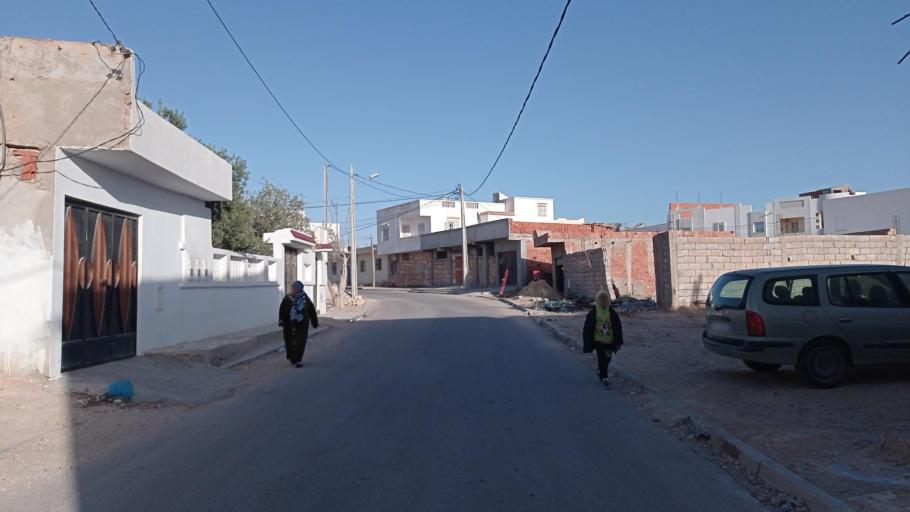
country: TN
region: Qabis
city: Gabes
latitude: 33.8566
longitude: 10.1188
